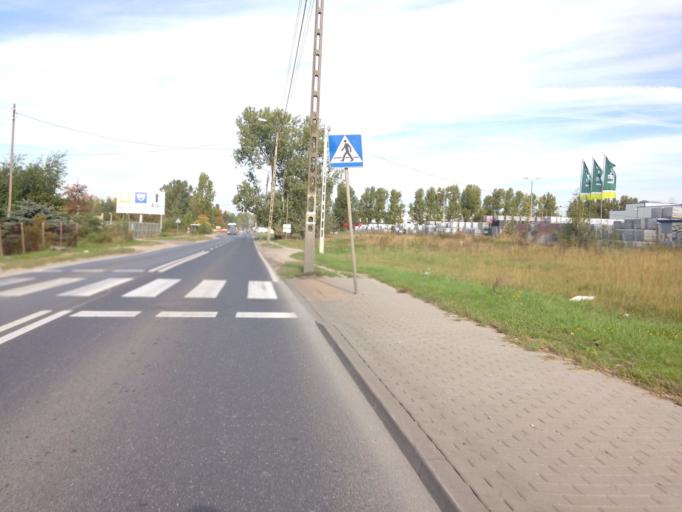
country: PL
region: Masovian Voivodeship
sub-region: Powiat wolominski
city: Zabki
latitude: 52.2660
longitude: 21.1215
